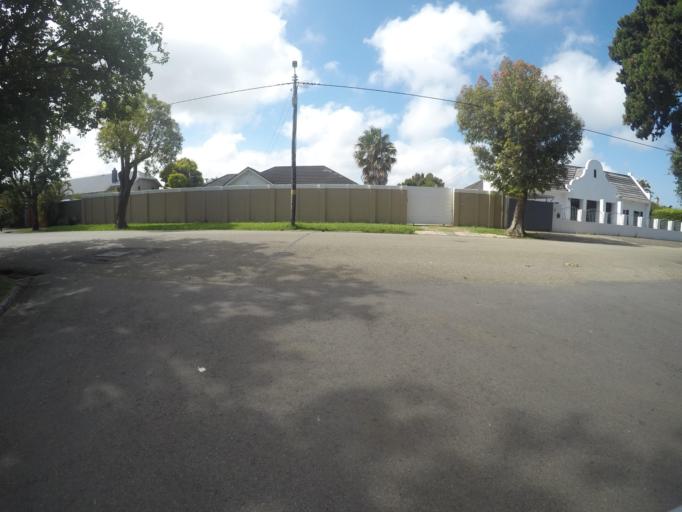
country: ZA
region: Eastern Cape
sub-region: Buffalo City Metropolitan Municipality
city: East London
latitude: -32.9793
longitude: 27.9127
